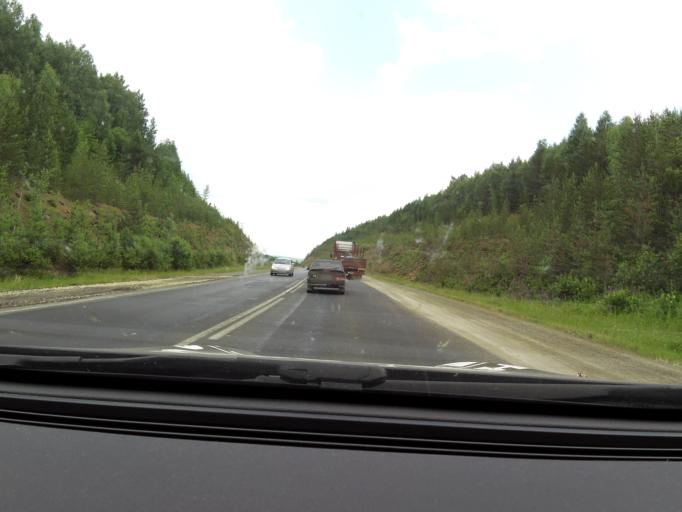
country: RU
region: Sverdlovsk
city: Ufimskiy
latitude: 56.7829
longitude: 58.3040
